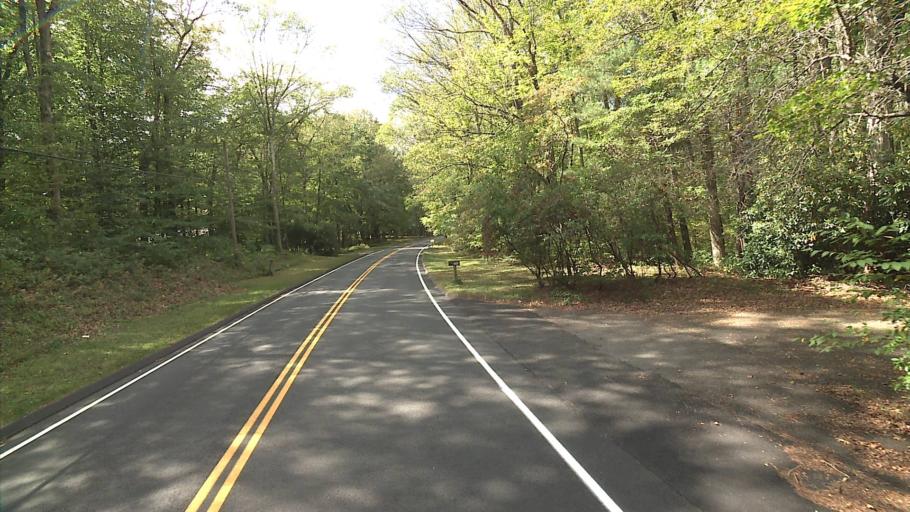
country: US
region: Connecticut
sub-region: Middlesex County
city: Higganum
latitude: 41.3885
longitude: -72.5676
